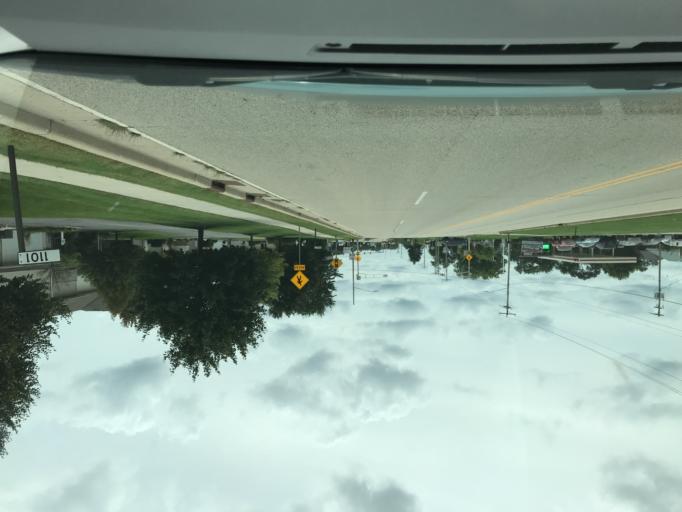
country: US
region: Wisconsin
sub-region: Racine County
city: Burlington
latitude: 42.6609
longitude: -88.2617
